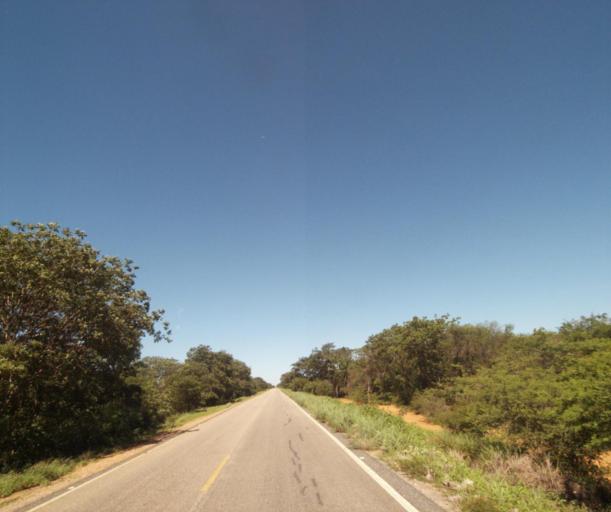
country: BR
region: Bahia
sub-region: Palmas De Monte Alto
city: Palmas de Monte Alto
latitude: -14.2614
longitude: -43.3085
